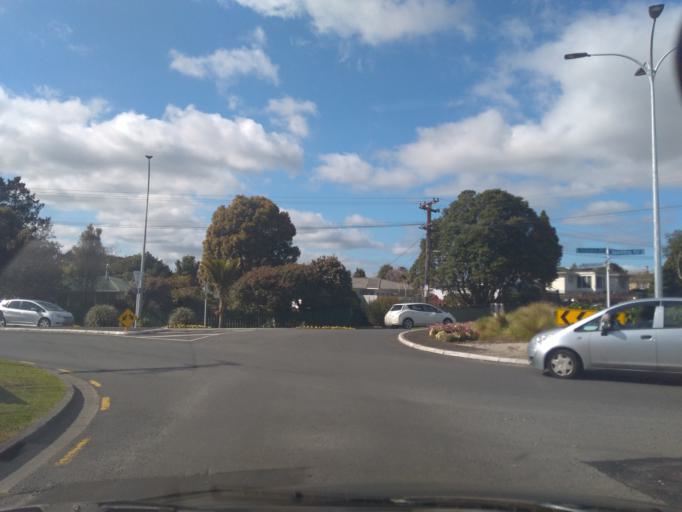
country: NZ
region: Northland
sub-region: Whangarei
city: Whangarei
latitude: -35.6861
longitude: 174.3266
